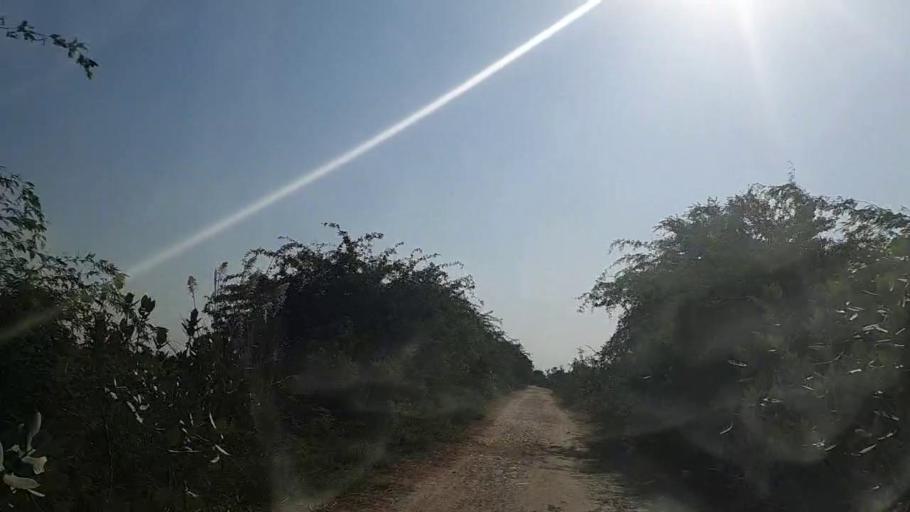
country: PK
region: Sindh
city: Mirpur Batoro
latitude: 24.6304
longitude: 68.1613
